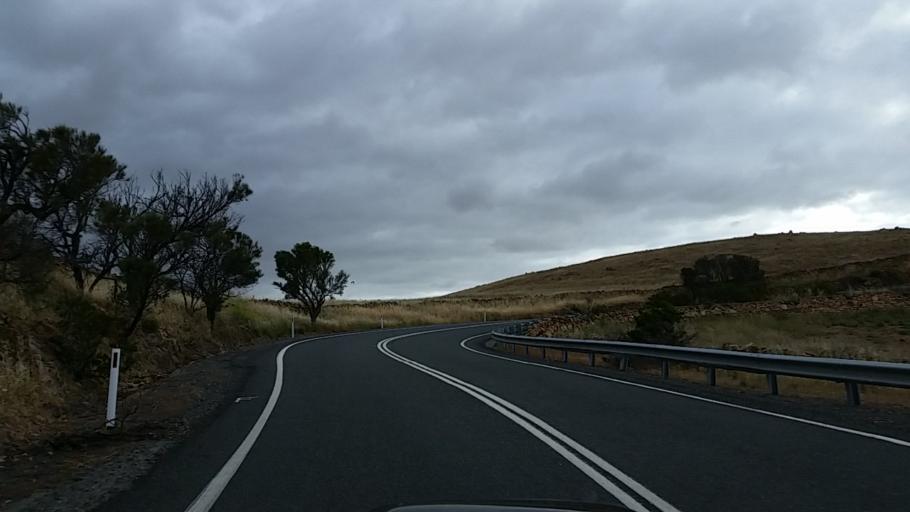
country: AU
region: South Australia
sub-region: Barossa
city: Angaston
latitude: -34.5626
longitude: 139.2150
